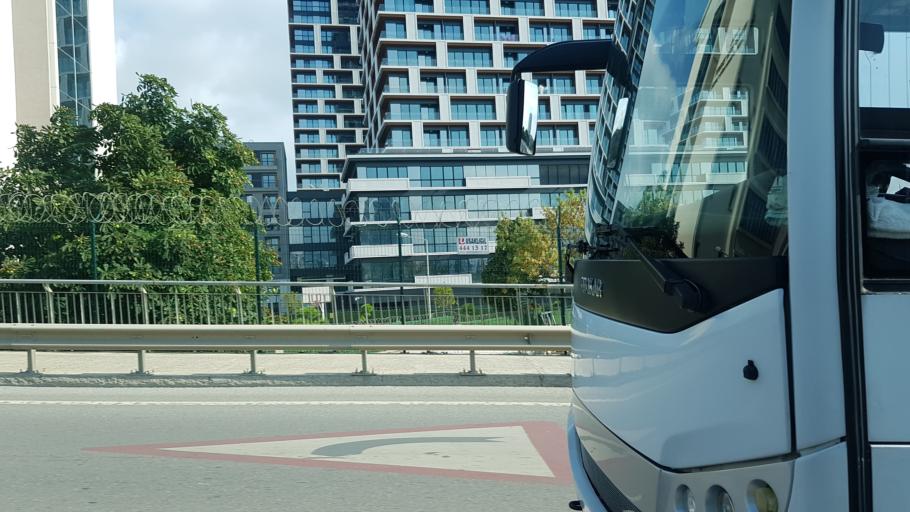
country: TR
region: Istanbul
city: Maltepe
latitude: 40.9110
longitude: 29.1862
